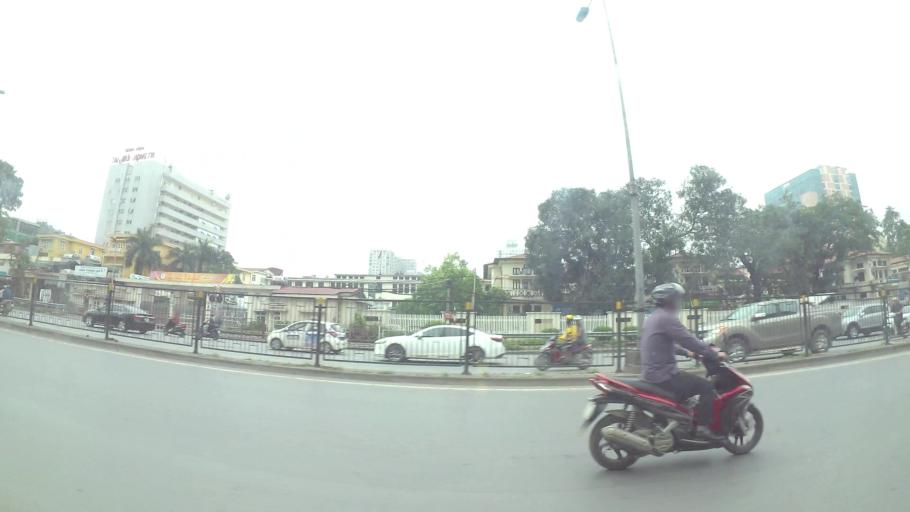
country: VN
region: Ha Noi
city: Hai BaTrung
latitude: 21.0007
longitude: 105.8414
